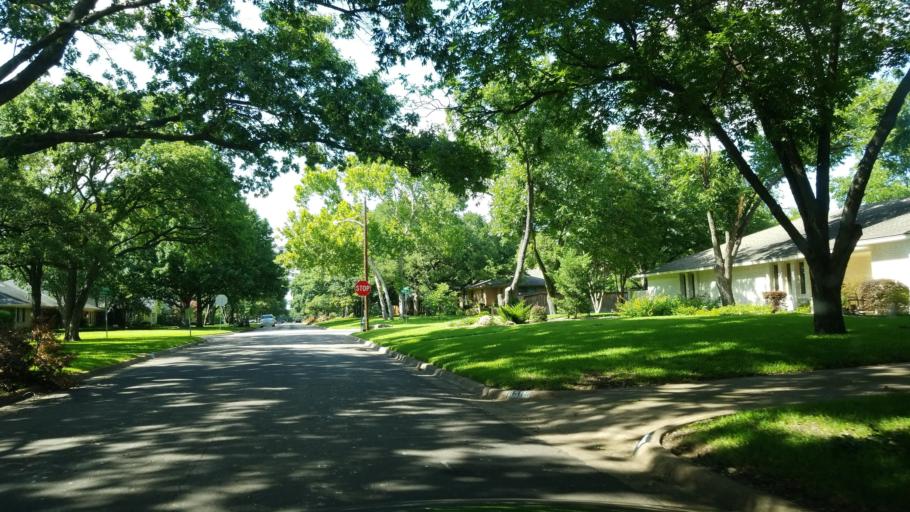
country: US
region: Texas
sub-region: Dallas County
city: University Park
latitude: 32.8830
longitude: -96.8498
